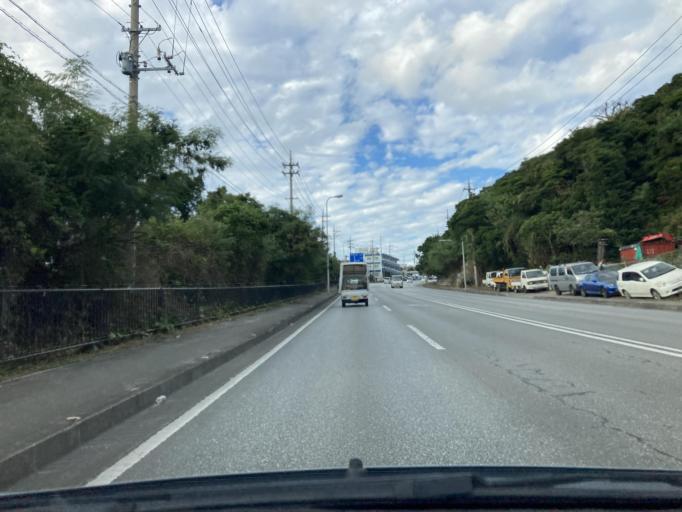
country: JP
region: Okinawa
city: Ishikawa
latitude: 26.4031
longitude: 127.8301
